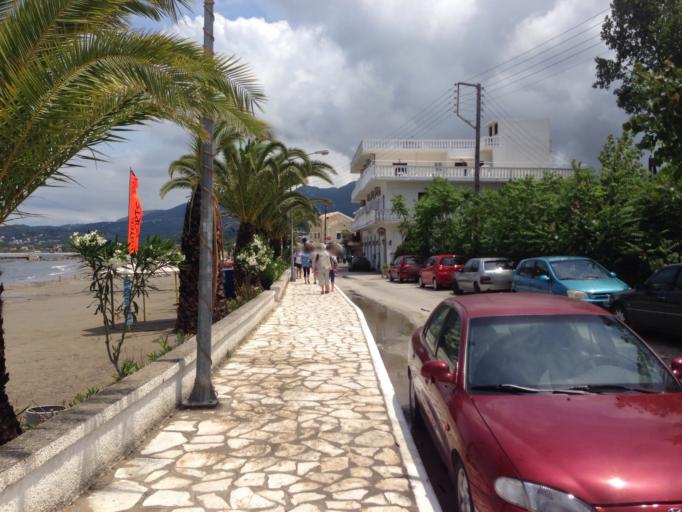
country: GR
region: Ionian Islands
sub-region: Nomos Kerkyras
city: Acharavi
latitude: 39.7913
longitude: 19.7876
